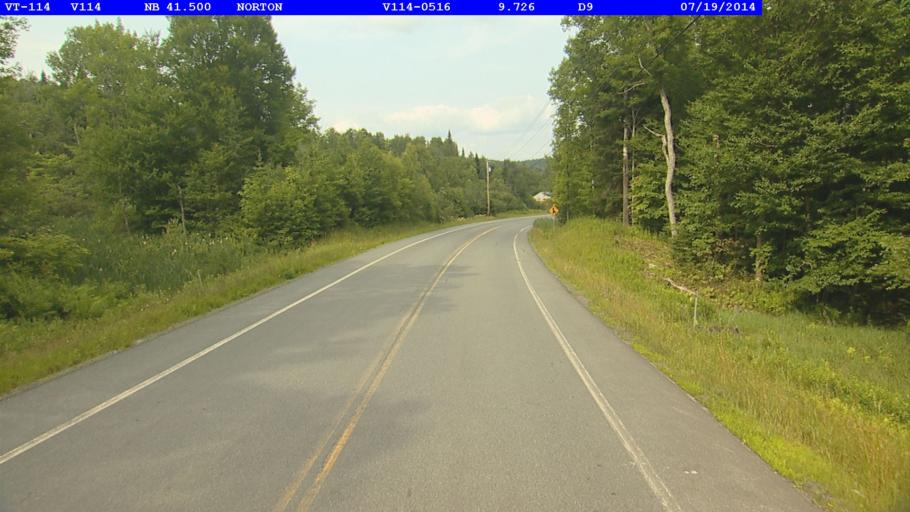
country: CA
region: Quebec
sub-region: Estrie
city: Coaticook
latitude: 44.9972
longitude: -71.7122
